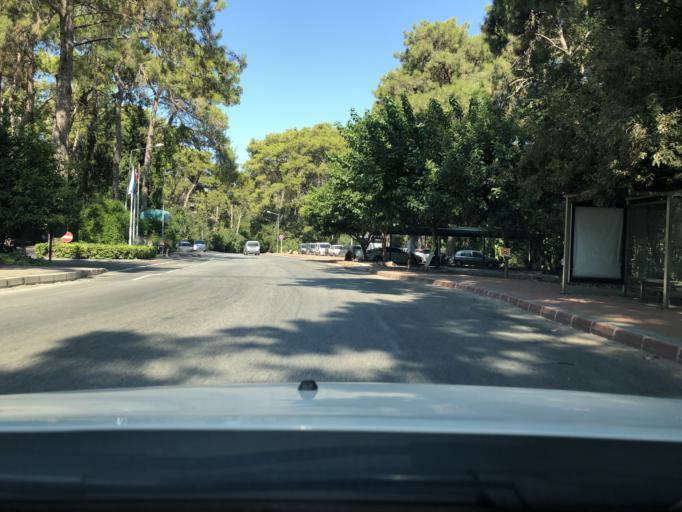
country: TR
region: Antalya
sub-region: Manavgat
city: Side
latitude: 36.7597
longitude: 31.4175
